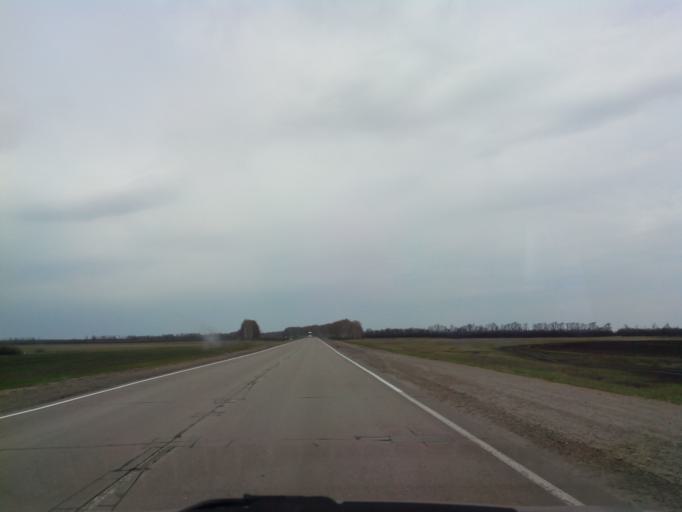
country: RU
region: Tambov
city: Znamenka
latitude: 52.2421
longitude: 41.5293
